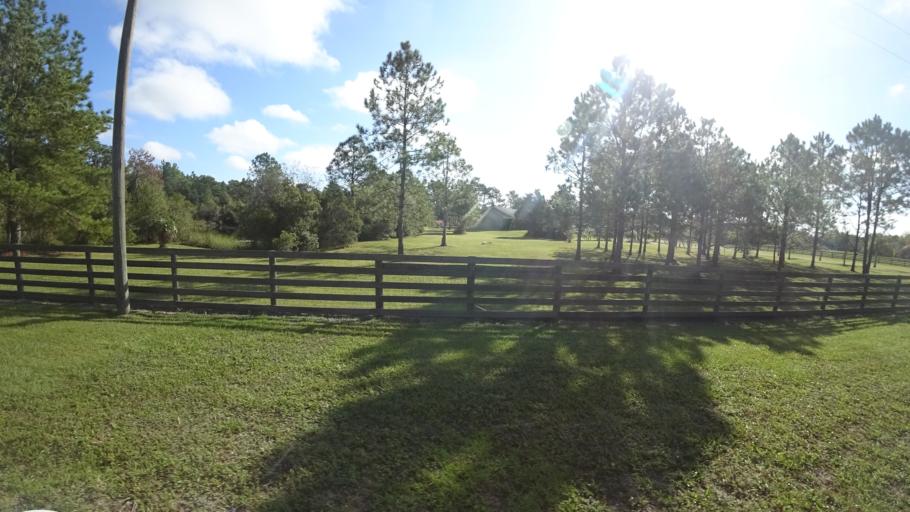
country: US
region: Florida
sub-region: Sarasota County
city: The Meadows
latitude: 27.4212
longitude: -82.3244
